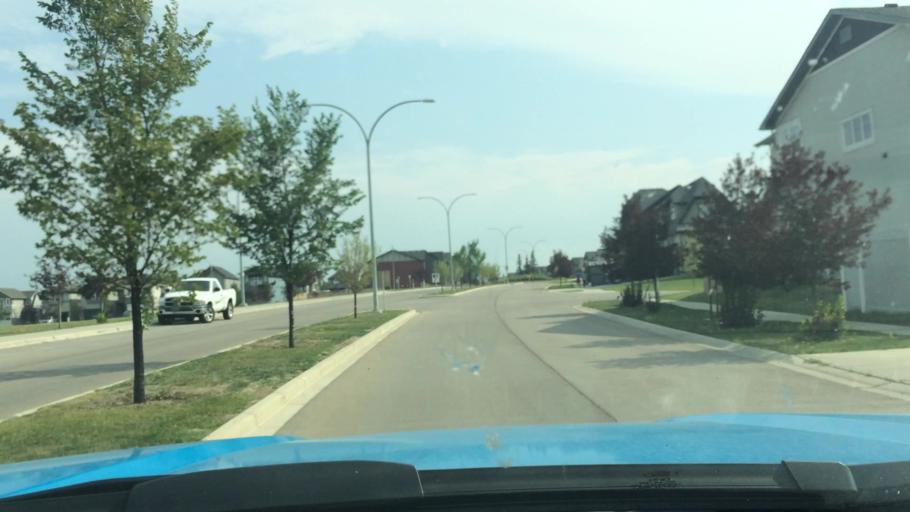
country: CA
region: Alberta
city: Calgary
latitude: 51.1813
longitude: -114.1538
